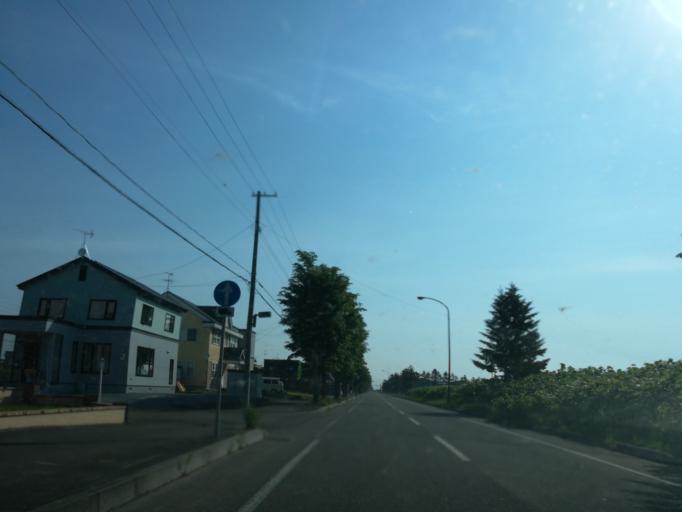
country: JP
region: Hokkaido
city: Iwamizawa
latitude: 43.1712
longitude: 141.7068
